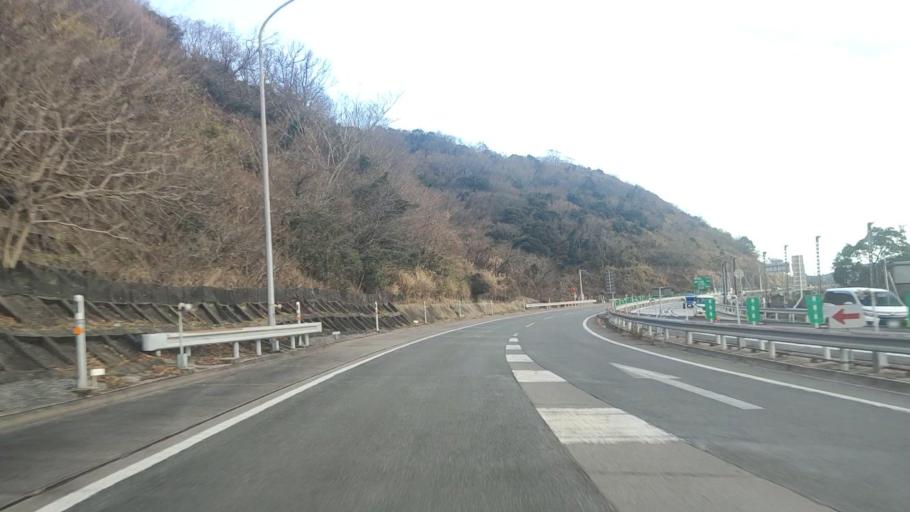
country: JP
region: Oita
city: Hiji
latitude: 33.3556
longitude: 131.4462
